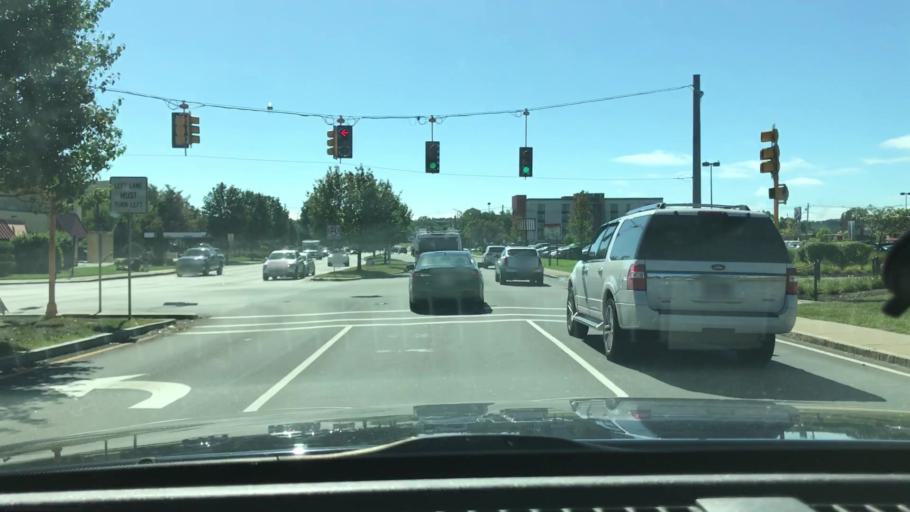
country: US
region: Massachusetts
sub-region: Middlesex County
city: Woburn
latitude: 42.5062
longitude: -71.1312
